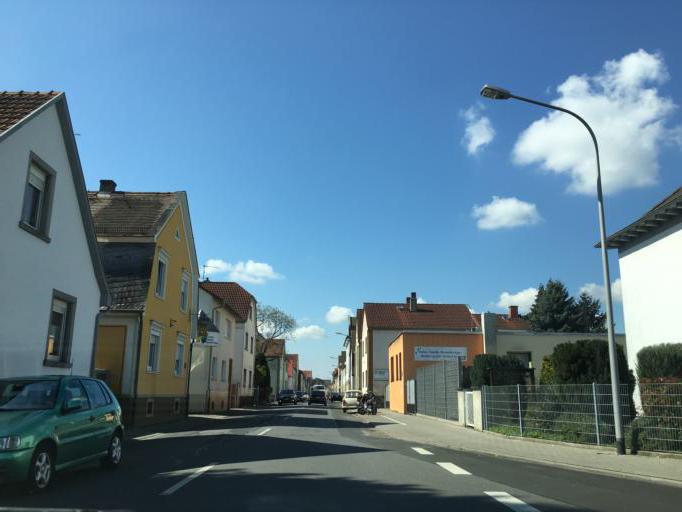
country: DE
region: Hesse
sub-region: Regierungsbezirk Darmstadt
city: Rodgau
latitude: 49.9982
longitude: 8.8783
